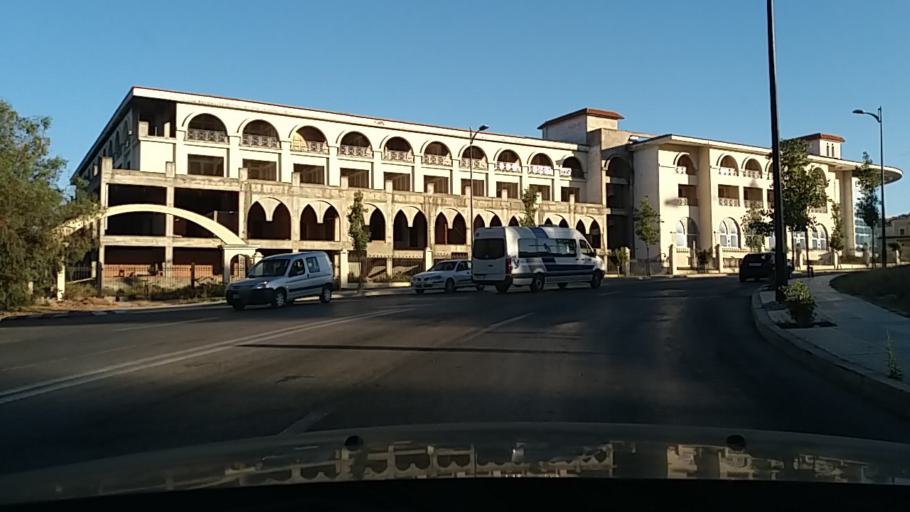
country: MA
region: Tanger-Tetouan
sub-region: Tanger-Assilah
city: Tangier
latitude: 35.7734
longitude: -5.8567
